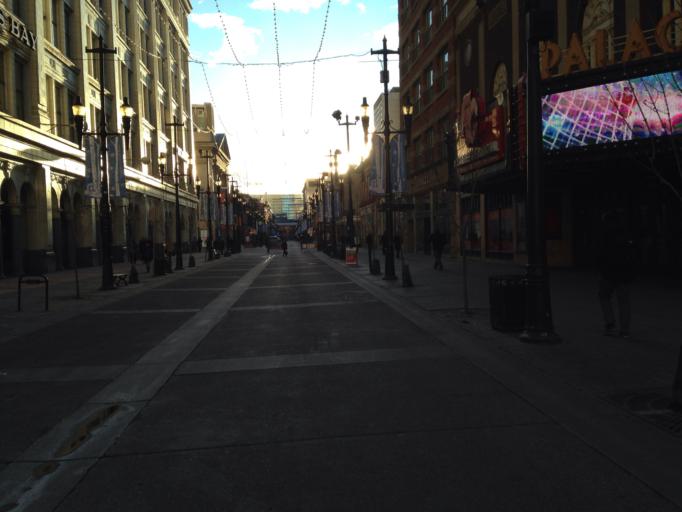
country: CA
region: Alberta
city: Calgary
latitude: 51.0457
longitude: -114.0669
